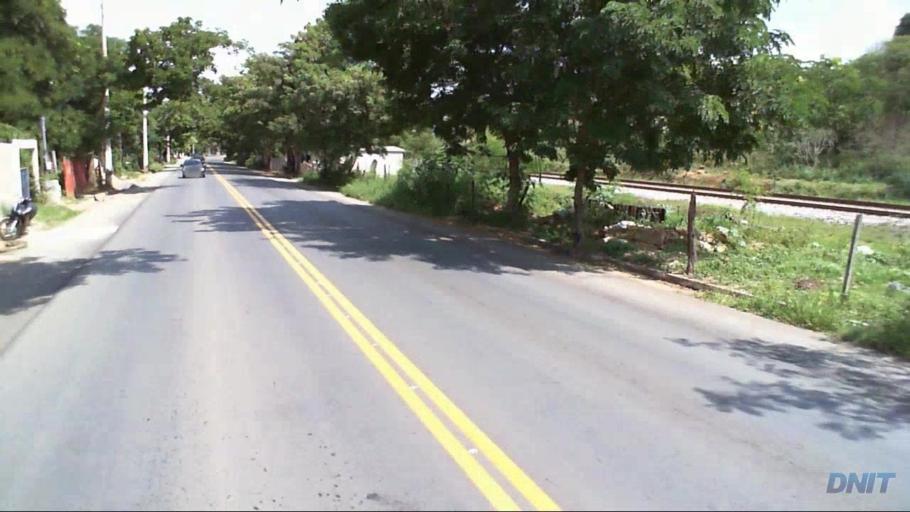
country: BR
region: Minas Gerais
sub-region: Governador Valadares
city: Governador Valadares
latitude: -18.9126
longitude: -41.9971
